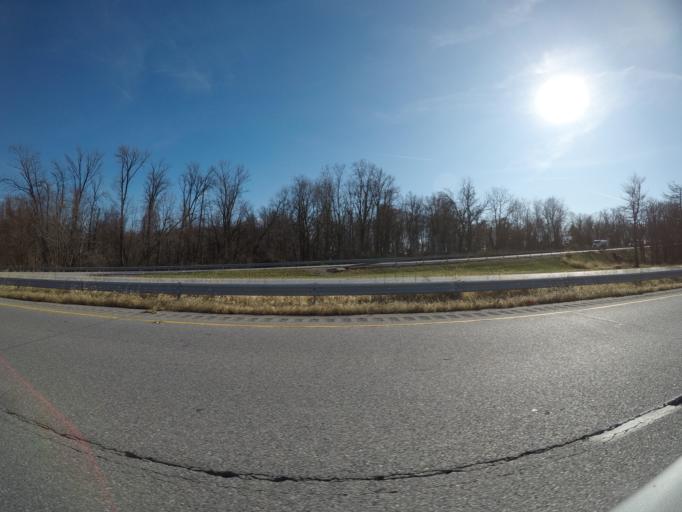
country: US
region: Pennsylvania
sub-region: Chester County
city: Coatesville
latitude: 39.9897
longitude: -75.8708
